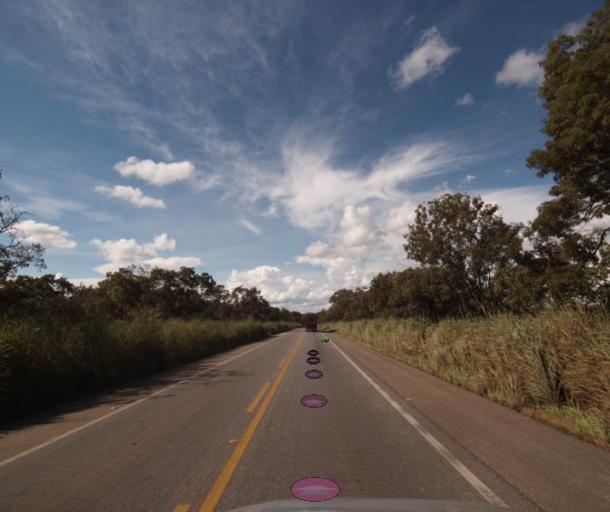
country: BR
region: Goias
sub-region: Porangatu
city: Porangatu
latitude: -12.9864
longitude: -49.1509
